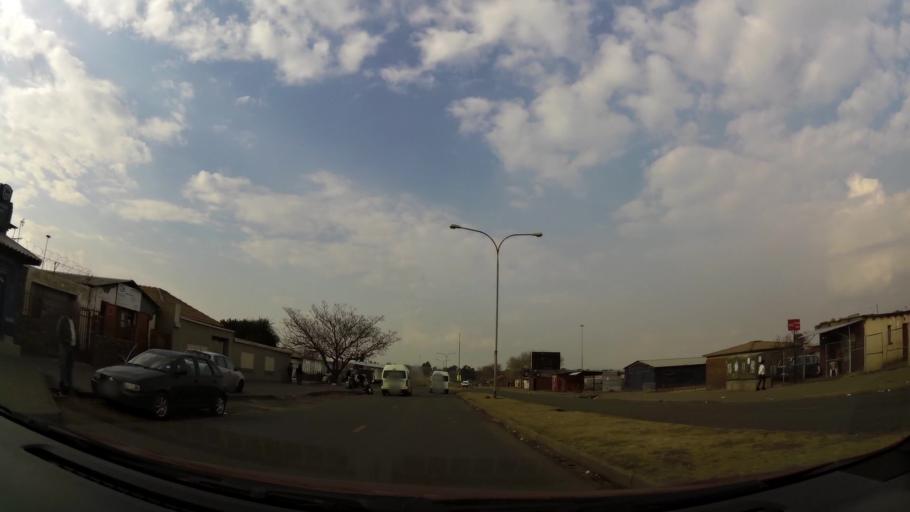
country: ZA
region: Gauteng
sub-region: Sedibeng District Municipality
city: Vereeniging
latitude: -26.6808
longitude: 27.8830
